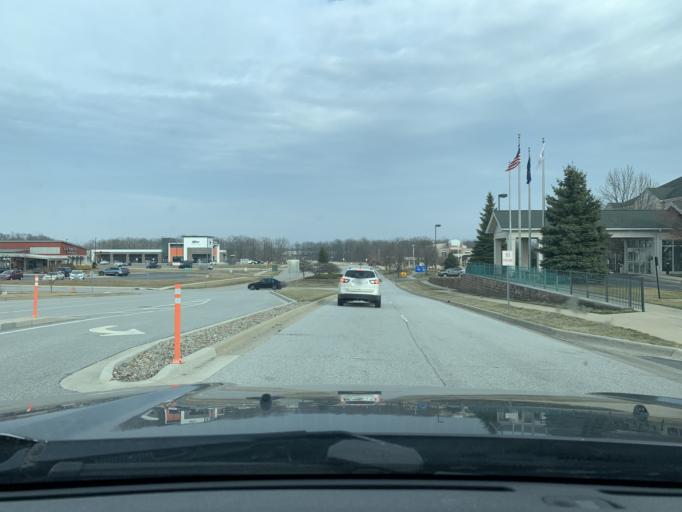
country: US
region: Indiana
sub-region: Porter County
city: Chesterton
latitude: 41.5760
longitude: -87.0447
